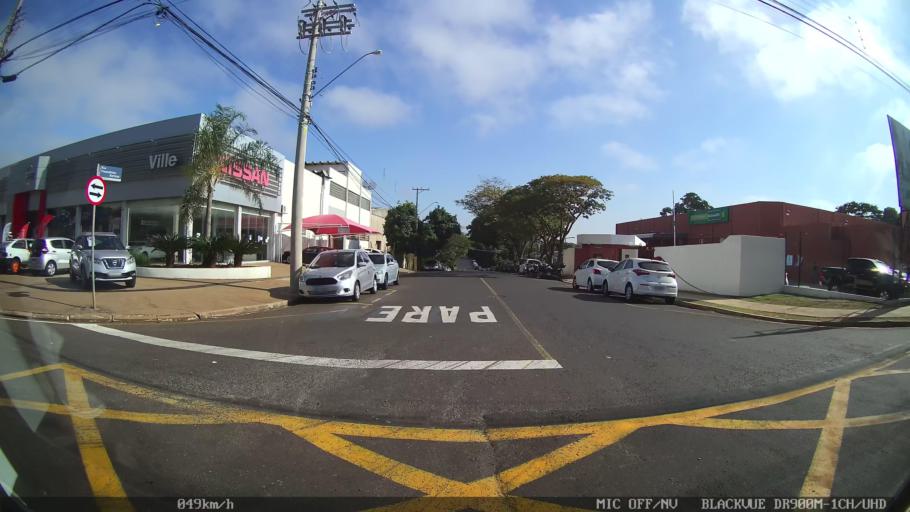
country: BR
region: Sao Paulo
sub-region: Sao Jose Do Rio Preto
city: Sao Jose do Rio Preto
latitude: -20.8214
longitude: -49.4168
